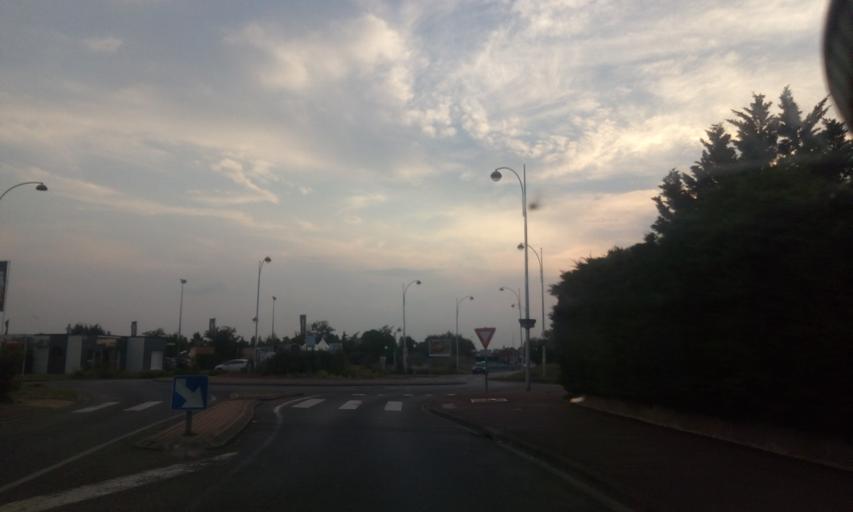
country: FR
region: Rhone-Alpes
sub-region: Departement du Rhone
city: Genas
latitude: 45.7348
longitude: 4.9831
